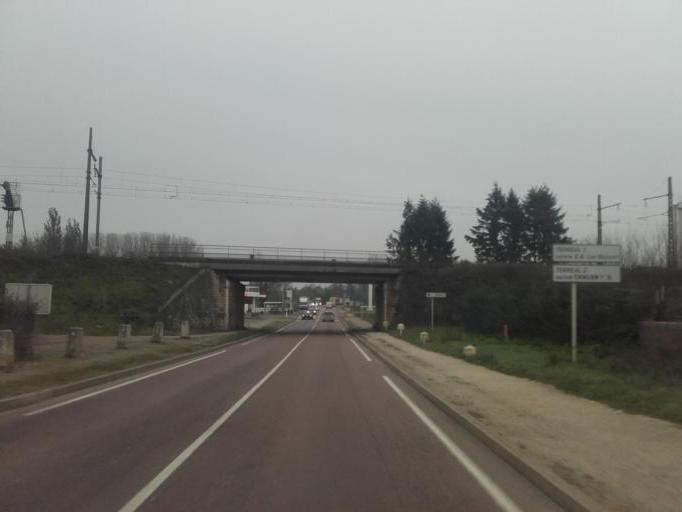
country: FR
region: Bourgogne
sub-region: Departement de Saone-et-Loire
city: Chagny
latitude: 46.9185
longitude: 4.7525
